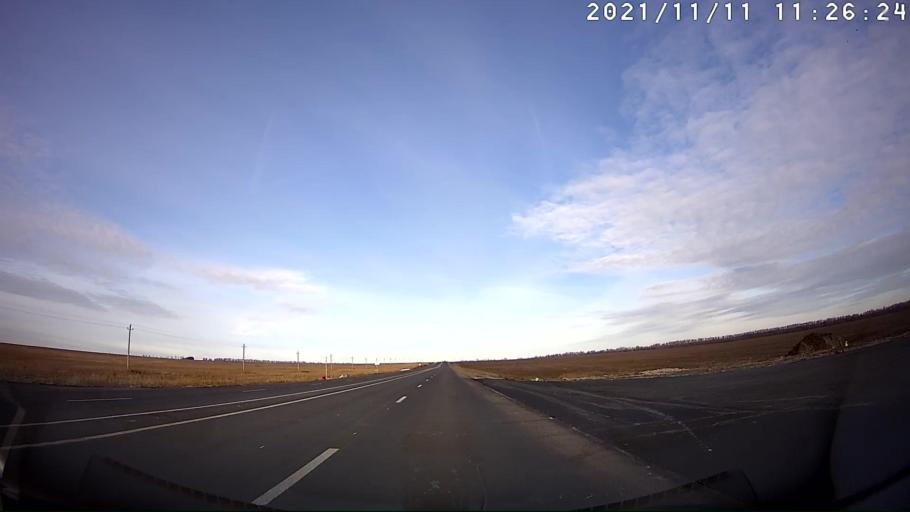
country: RU
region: Samara
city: Syzran'
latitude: 53.2345
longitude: 48.4924
